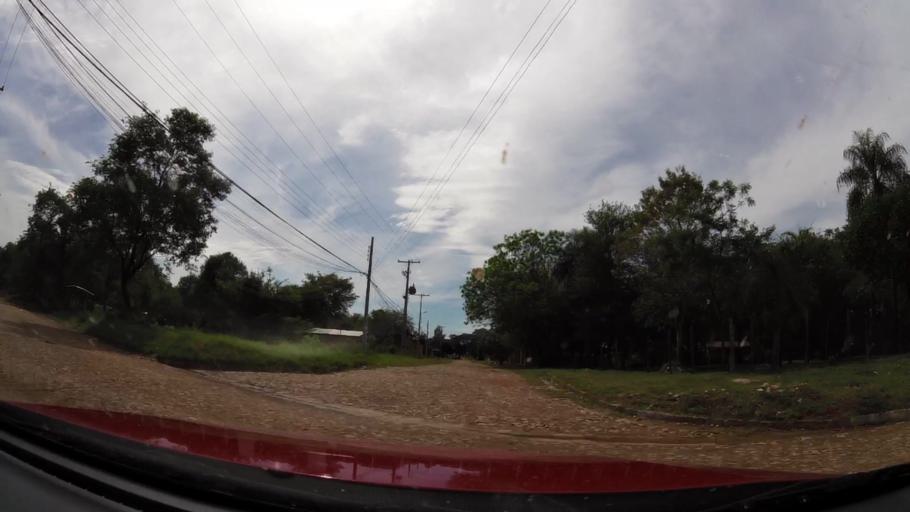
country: PY
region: Central
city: Limpio
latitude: -25.1888
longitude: -57.4744
